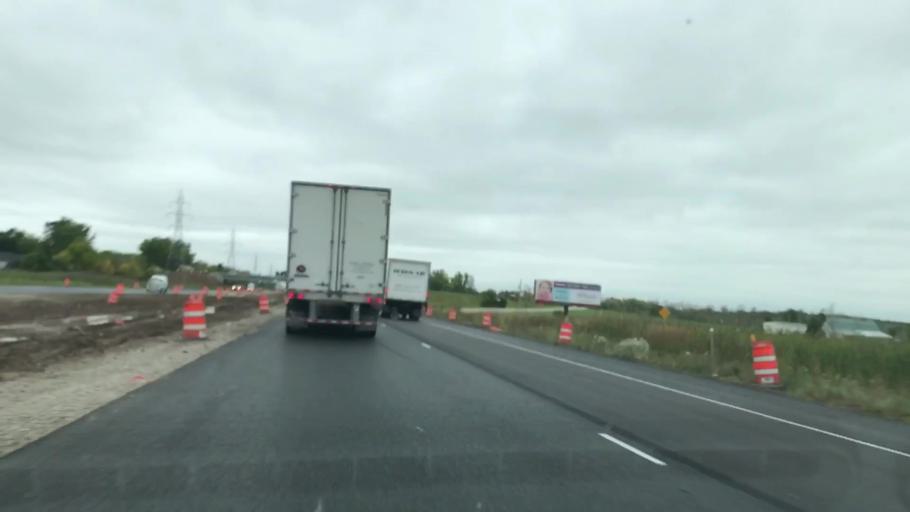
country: US
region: Wisconsin
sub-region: Brown County
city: Suamico
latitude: 44.6239
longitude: -88.0501
